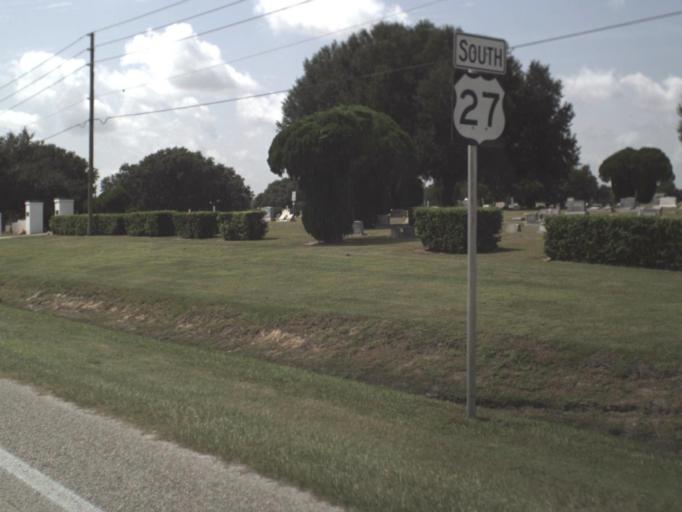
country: US
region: Florida
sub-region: Polk County
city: Lake Wales
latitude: 27.8958
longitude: -81.5999
